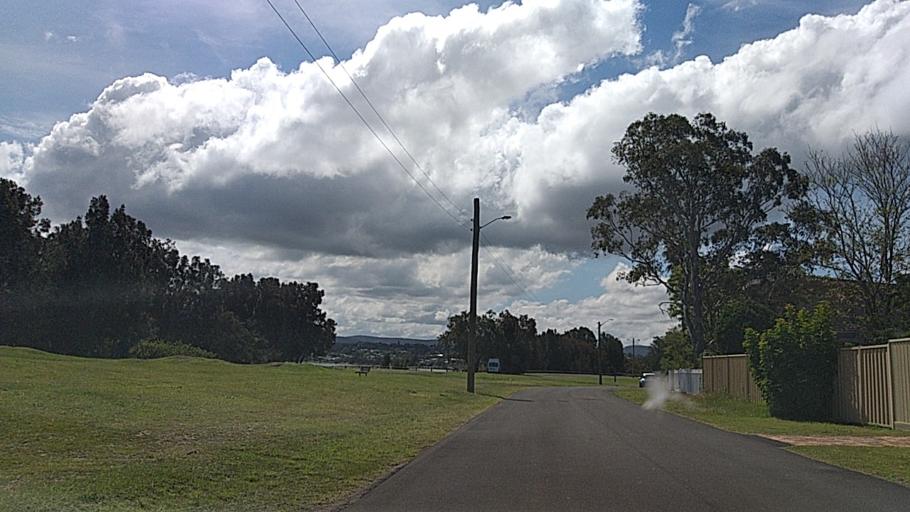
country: AU
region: New South Wales
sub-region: Wollongong
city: Lake Heights
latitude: -34.5018
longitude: 150.8738
